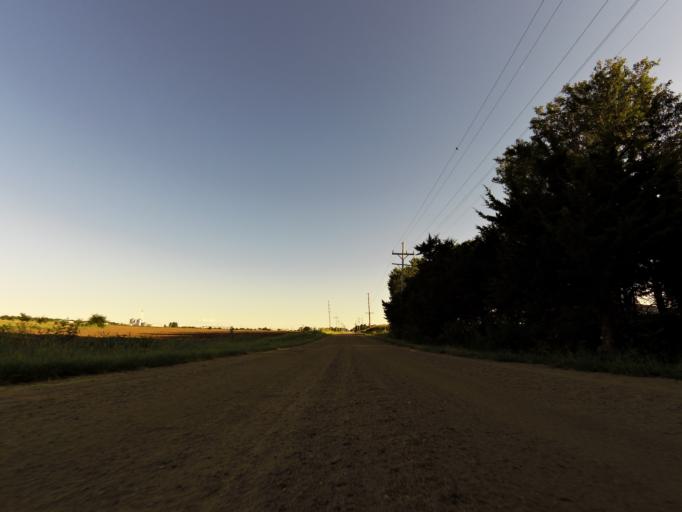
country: US
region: Kansas
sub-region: Reno County
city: South Hutchinson
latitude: 38.0053
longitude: -98.0319
